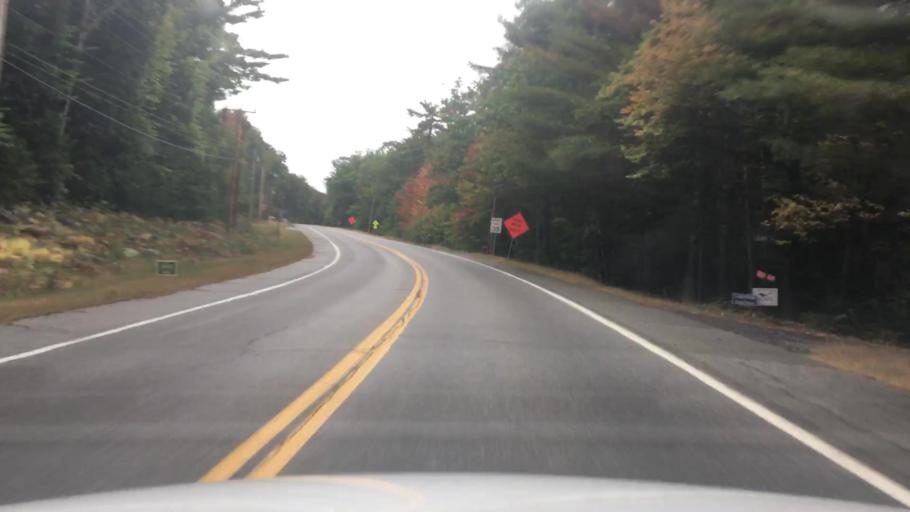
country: US
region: Maine
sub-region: Kennebec County
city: Rome
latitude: 44.5221
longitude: -69.8806
